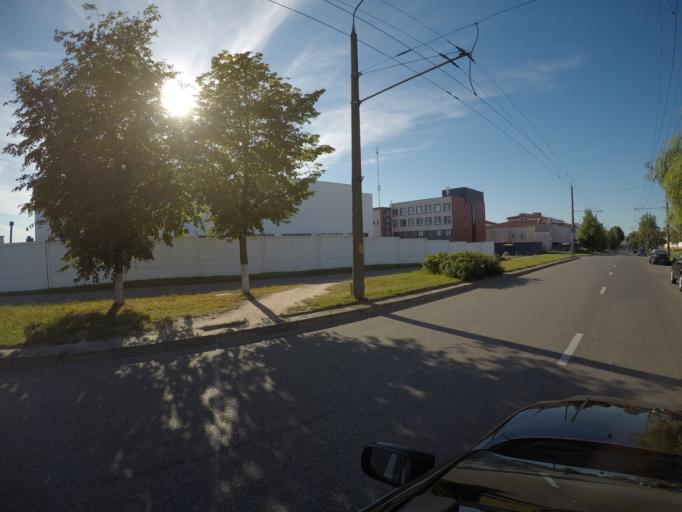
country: BY
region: Grodnenskaya
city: Hrodna
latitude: 53.7101
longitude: 23.8271
